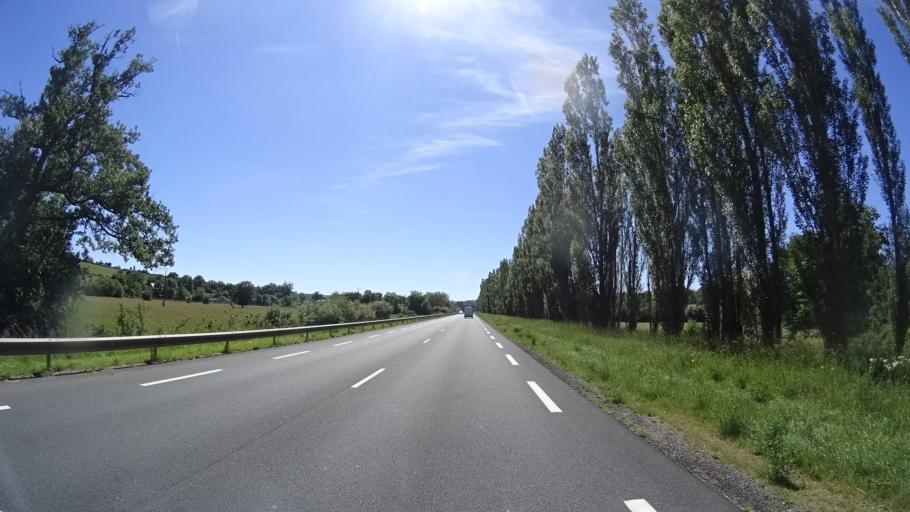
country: FR
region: Midi-Pyrenees
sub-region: Departement de l'Aveyron
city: Sebazac-Concoures
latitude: 44.3745
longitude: 2.6003
